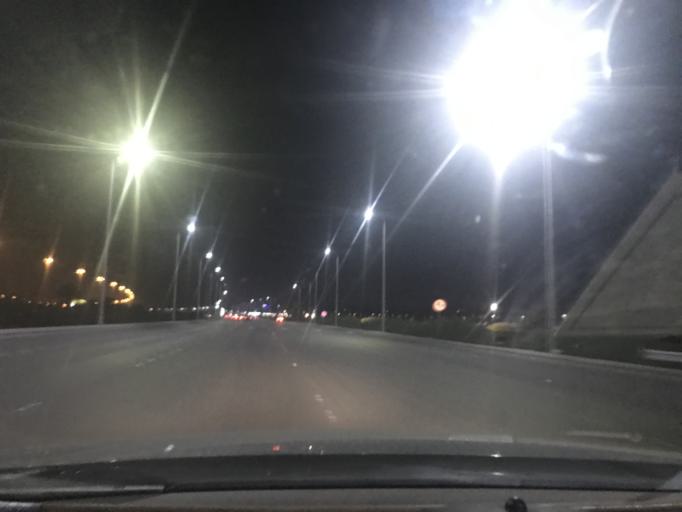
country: SA
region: Ar Riyad
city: Riyadh
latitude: 24.8400
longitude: 46.7302
